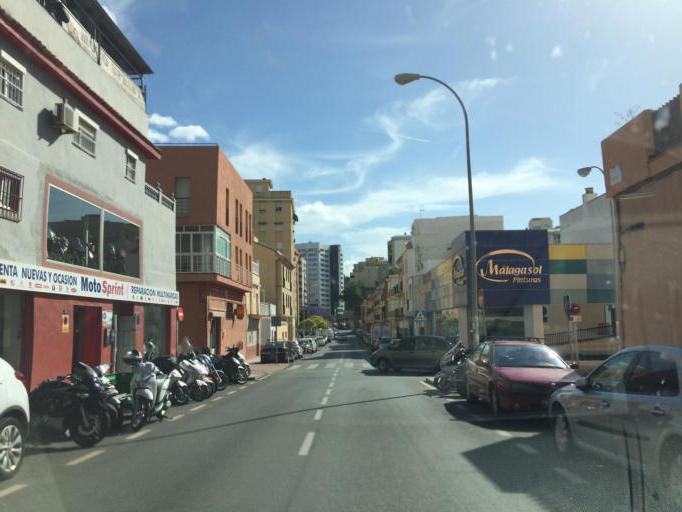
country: ES
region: Andalusia
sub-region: Provincia de Malaga
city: Malaga
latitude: 36.7135
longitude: -4.4389
